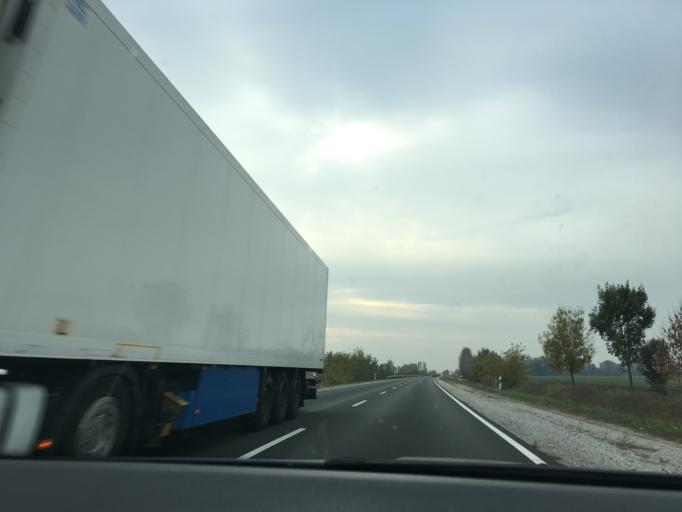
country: HU
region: Pest
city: Abony
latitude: 47.2039
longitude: 19.9562
